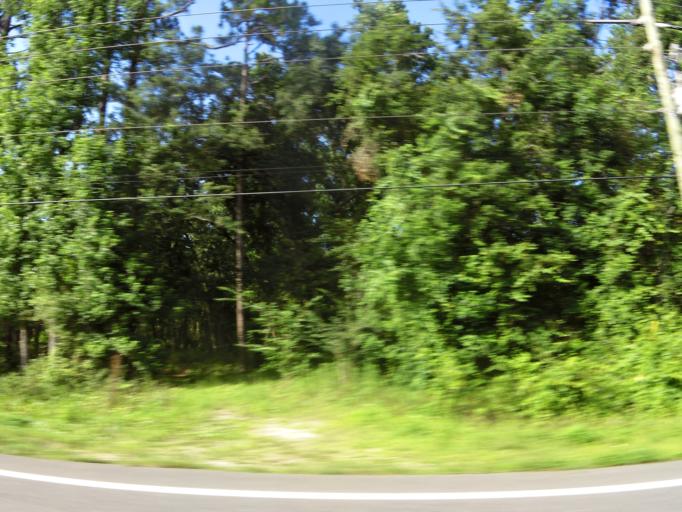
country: US
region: Florida
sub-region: Clay County
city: Green Cove Springs
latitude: 30.0129
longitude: -81.5585
